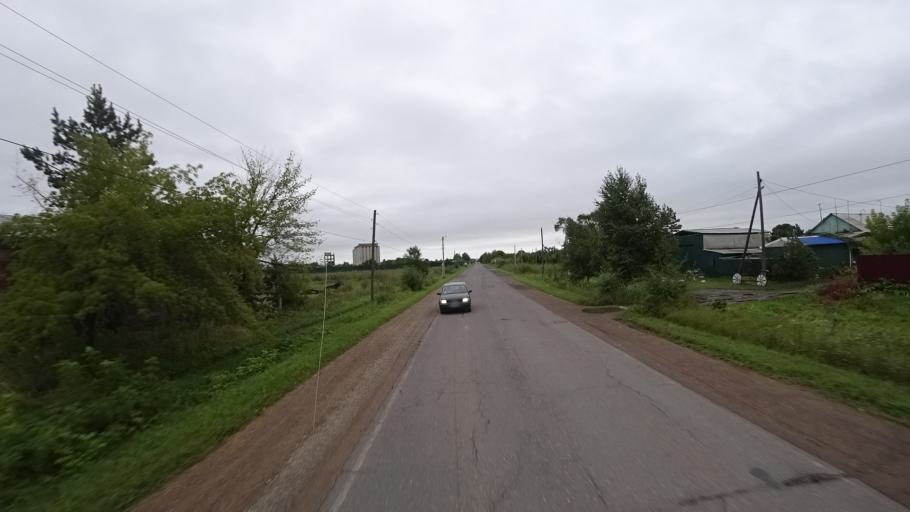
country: RU
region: Primorskiy
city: Chernigovka
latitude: 44.3421
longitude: 132.5401
